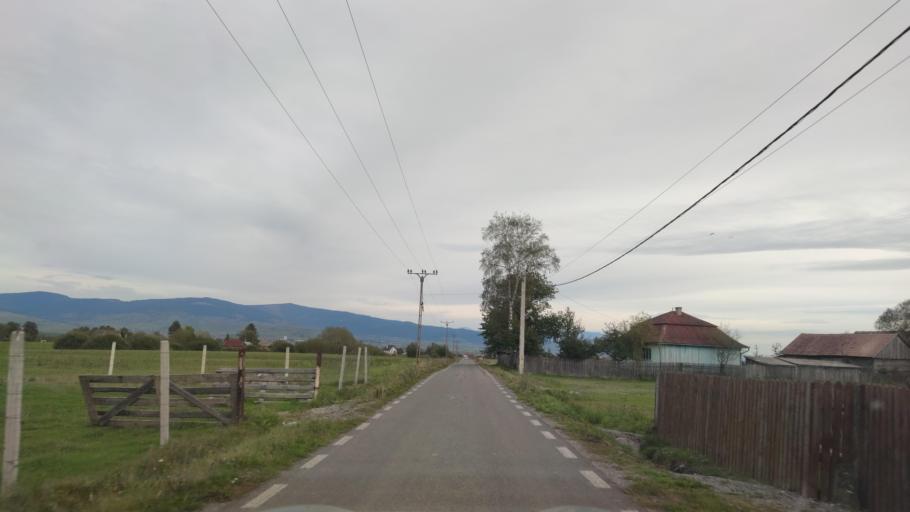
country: RO
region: Harghita
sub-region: Comuna Remetea
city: Remetea
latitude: 46.8094
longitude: 25.4273
